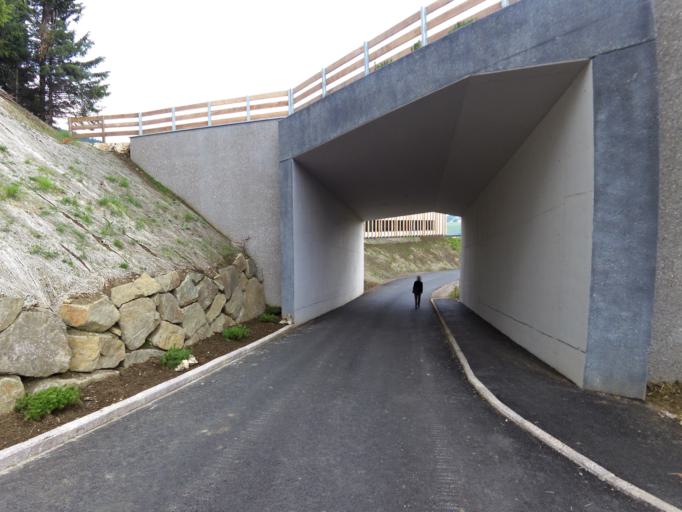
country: IT
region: Trentino-Alto Adige
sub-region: Bolzano
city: Siusi
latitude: 46.5434
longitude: 11.6168
